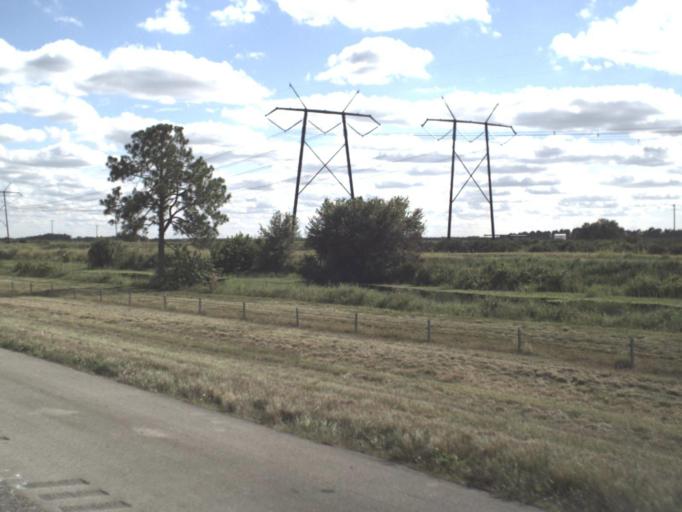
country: US
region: Florida
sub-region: Indian River County
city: West Vero Corridor
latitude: 27.5041
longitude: -80.5837
